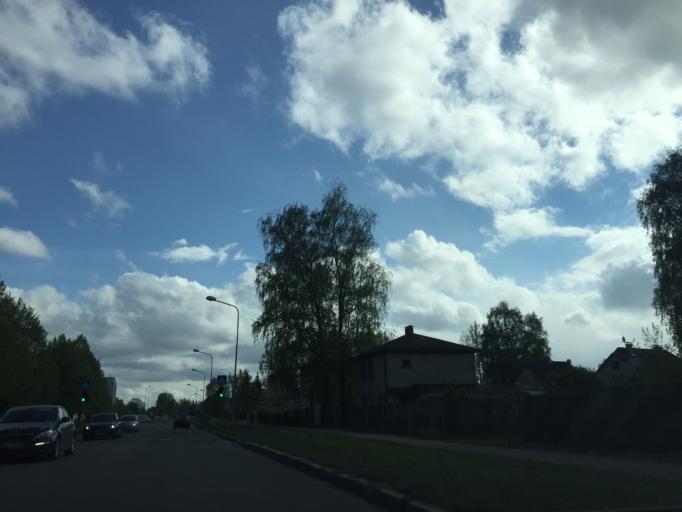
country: LV
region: Riga
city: Riga
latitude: 56.9439
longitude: 24.1956
